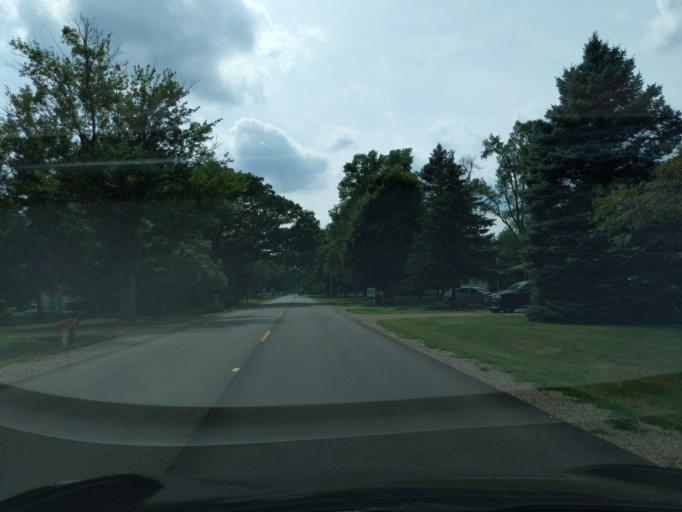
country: US
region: Michigan
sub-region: Eaton County
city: Eaton Rapids
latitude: 42.5094
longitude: -84.6160
